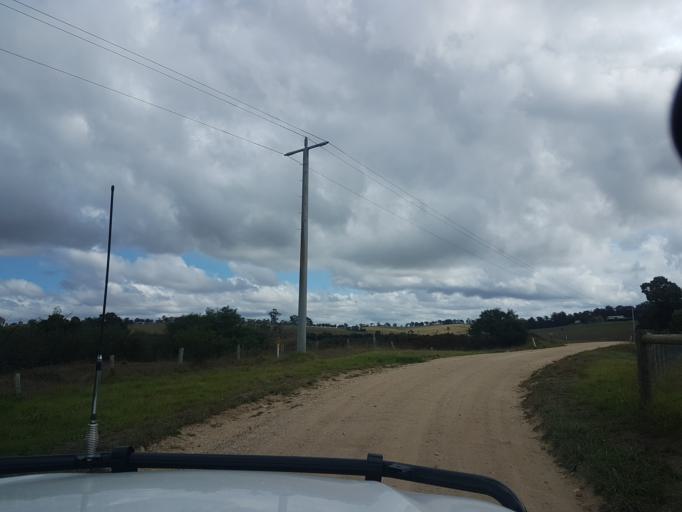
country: AU
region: Victoria
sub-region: East Gippsland
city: Bairnsdale
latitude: -37.7856
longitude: 147.5474
